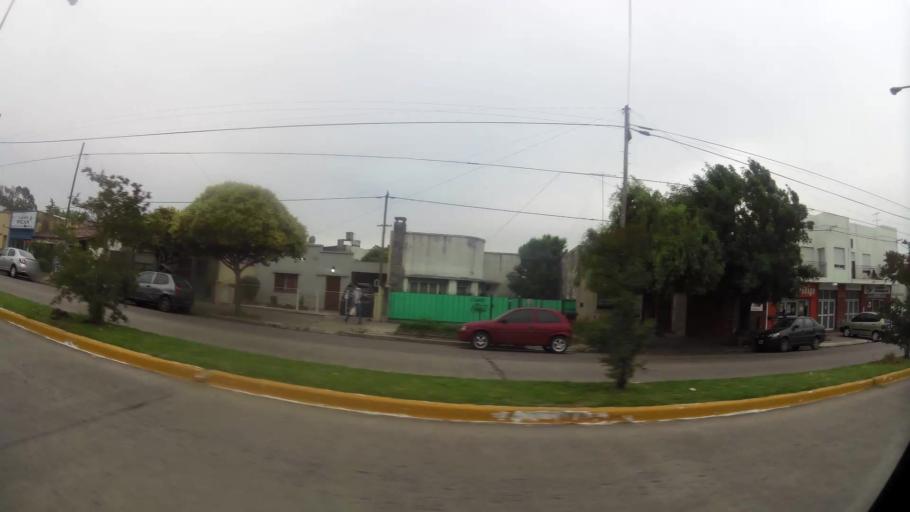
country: AR
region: Buenos Aires
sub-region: Partido de La Plata
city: La Plata
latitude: -34.9226
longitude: -57.9880
